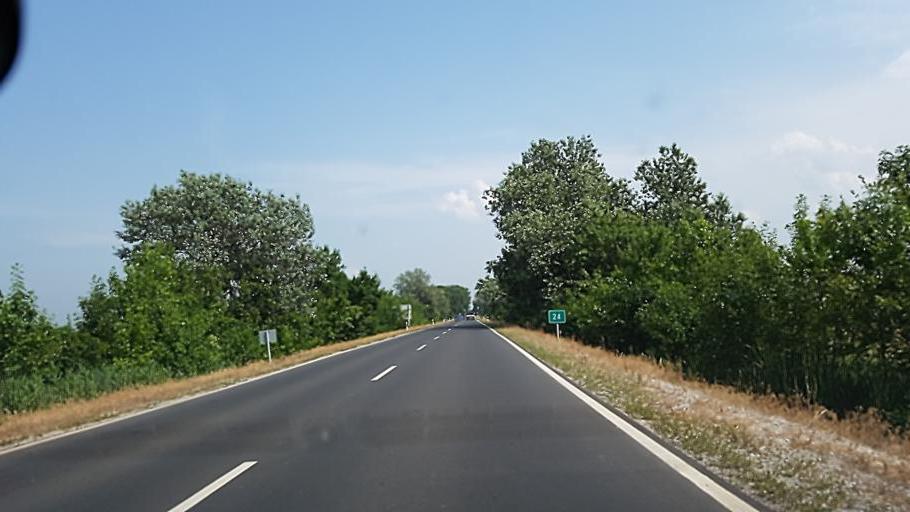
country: HU
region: Heves
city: Poroszlo
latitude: 47.6486
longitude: 20.6253
